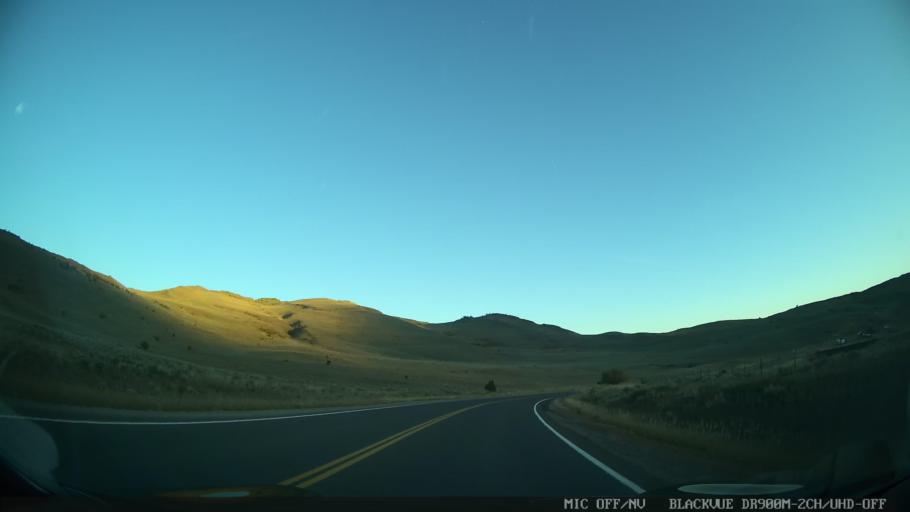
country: US
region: Colorado
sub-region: Eagle County
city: Edwards
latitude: 39.8116
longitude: -106.6750
